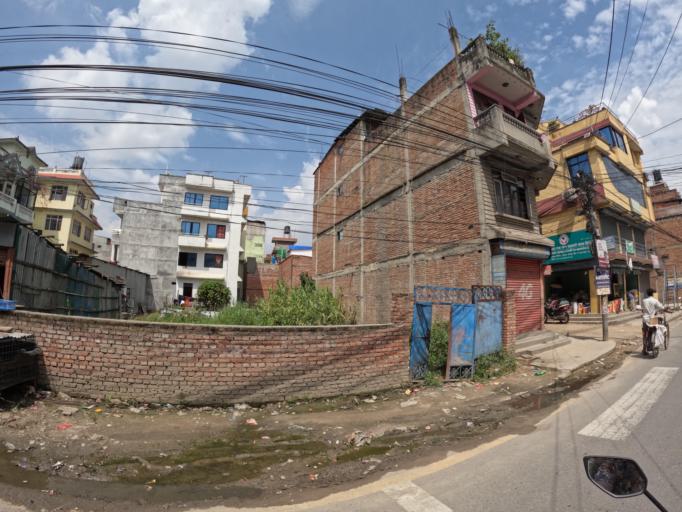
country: NP
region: Central Region
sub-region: Bagmati Zone
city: Bhaktapur
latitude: 27.6751
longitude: 85.3745
